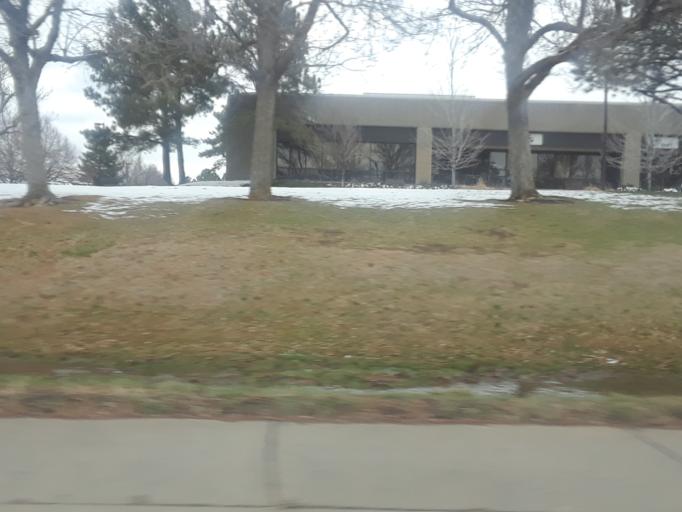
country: US
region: Colorado
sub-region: Arapahoe County
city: Centennial
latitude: 39.5661
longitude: -104.8820
